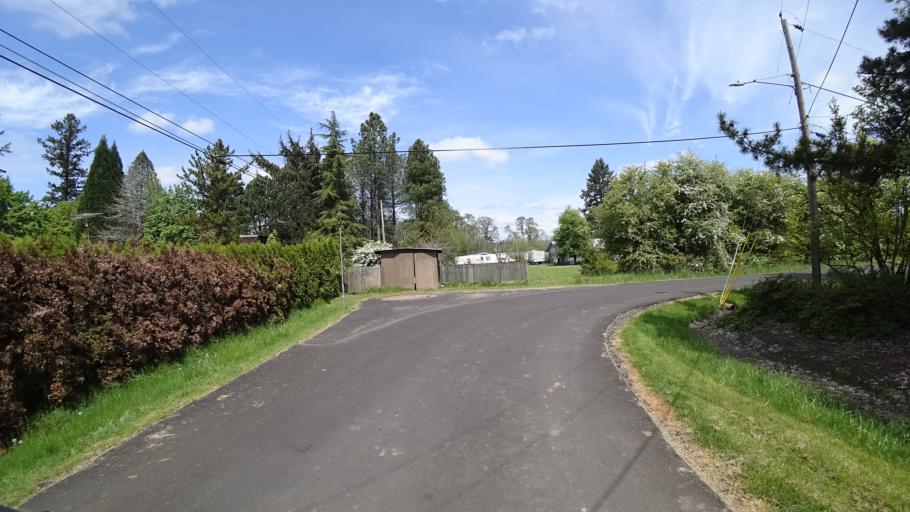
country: US
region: Oregon
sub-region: Washington County
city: Rockcreek
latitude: 45.5642
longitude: -122.9308
